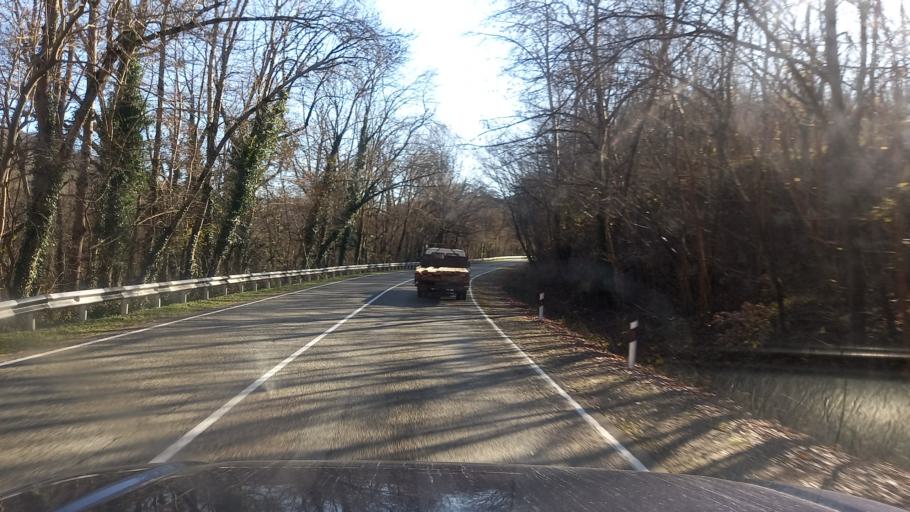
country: RU
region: Krasnodarskiy
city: Goryachiy Klyuch
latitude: 44.6057
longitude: 39.0814
